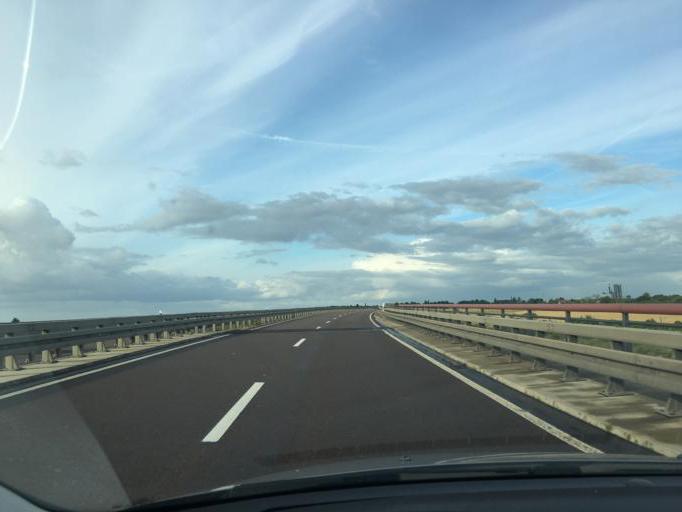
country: DE
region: Saxony-Anhalt
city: Bernburg
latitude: 51.8082
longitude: 11.7059
